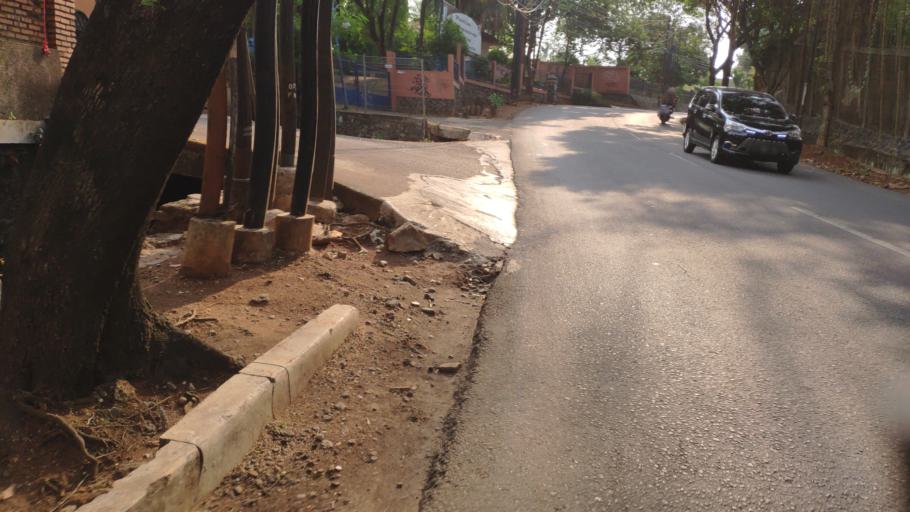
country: ID
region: West Java
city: Pamulang
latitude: -6.3109
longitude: 106.8116
